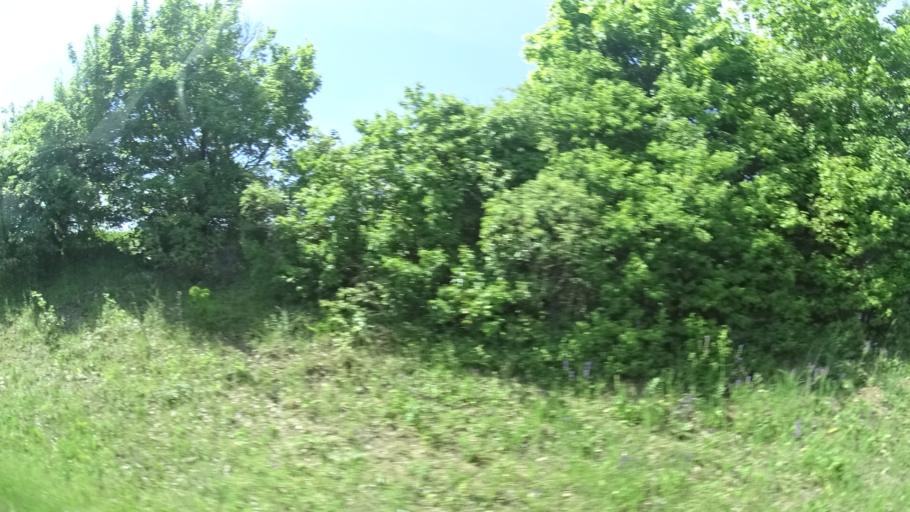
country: DE
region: Bavaria
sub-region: Regierungsbezirk Unterfranken
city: Oerlenbach
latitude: 50.1761
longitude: 10.1537
